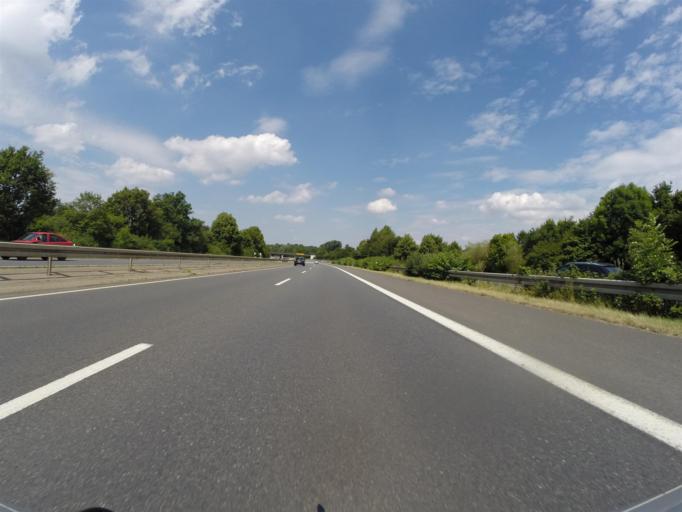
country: DE
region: Lower Saxony
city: Laatzen
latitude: 52.3518
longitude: 9.7932
